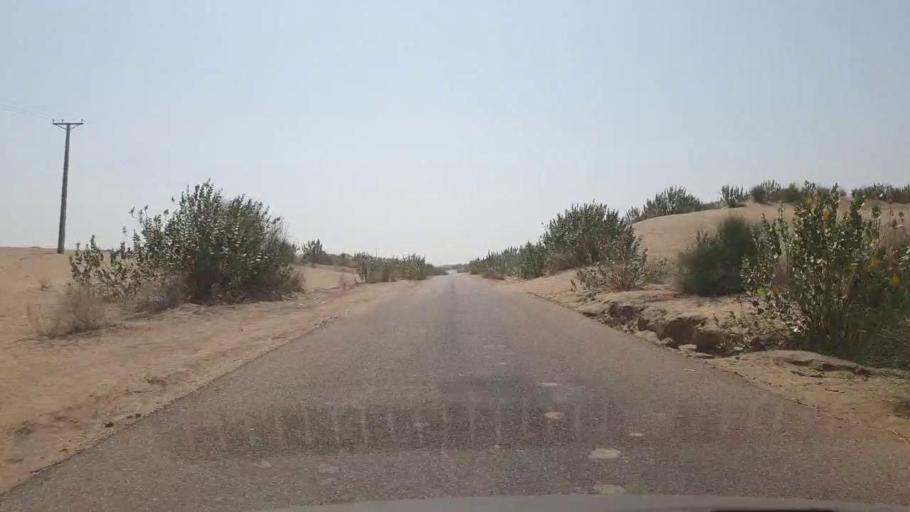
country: PK
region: Sindh
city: Chor
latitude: 25.6575
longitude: 70.1672
